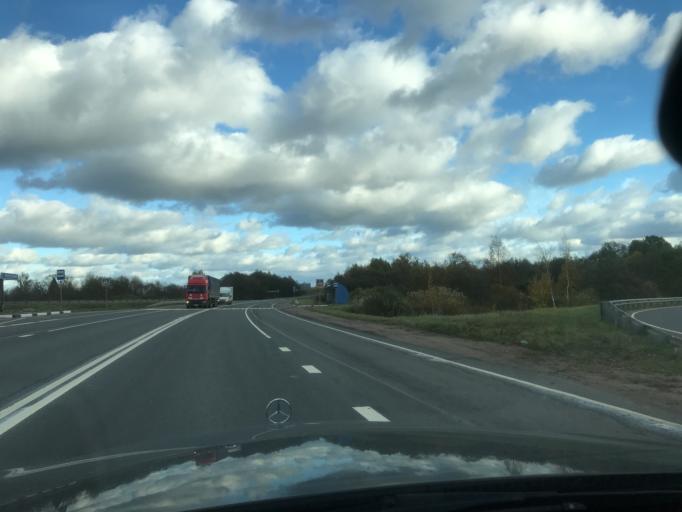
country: RU
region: Pskov
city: Novosokol'niki
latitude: 56.3207
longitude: 30.1376
